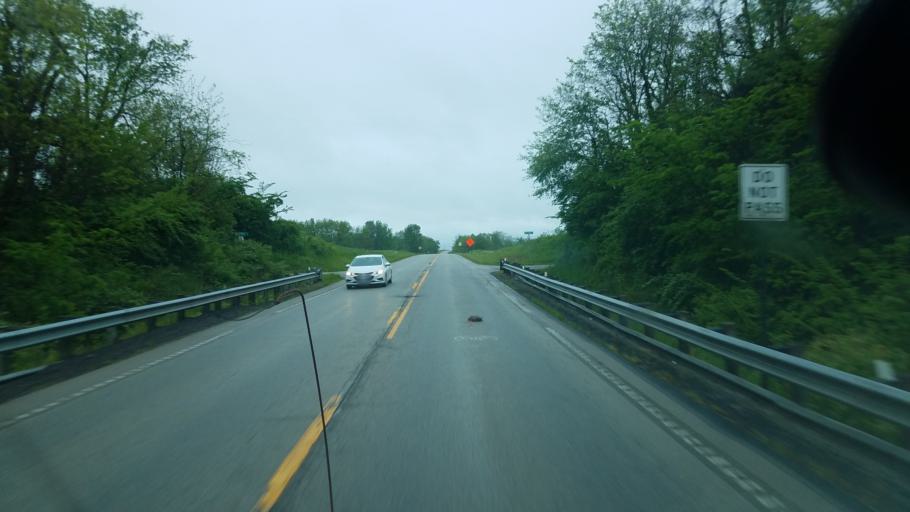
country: US
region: Ohio
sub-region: Highland County
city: Leesburg
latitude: 39.2978
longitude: -83.5847
